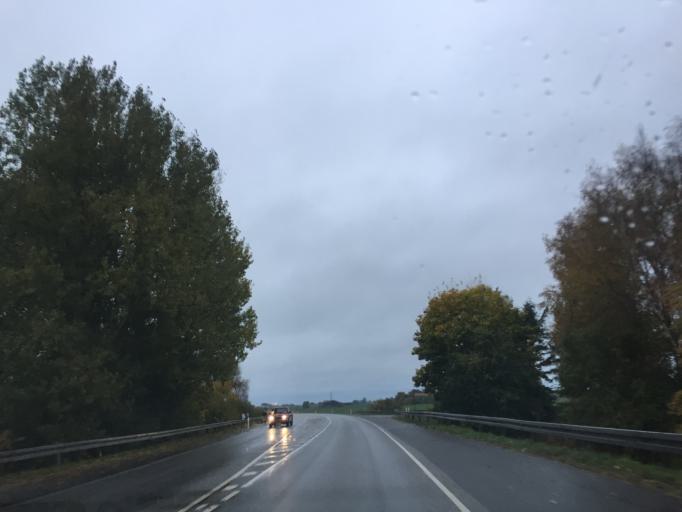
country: DK
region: Zealand
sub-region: Ringsted Kommune
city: Ringsted
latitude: 55.4778
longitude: 11.7386
